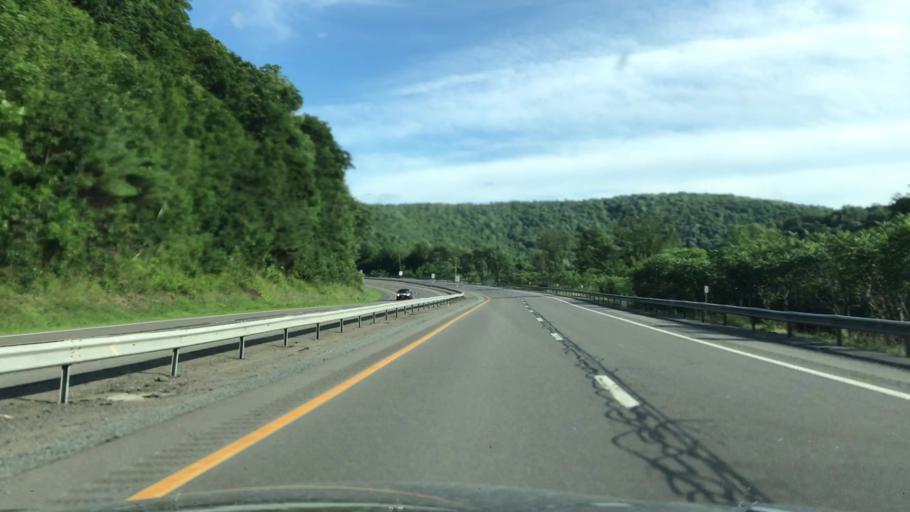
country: US
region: New York
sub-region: Delaware County
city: Hancock
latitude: 41.9747
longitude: -75.3377
